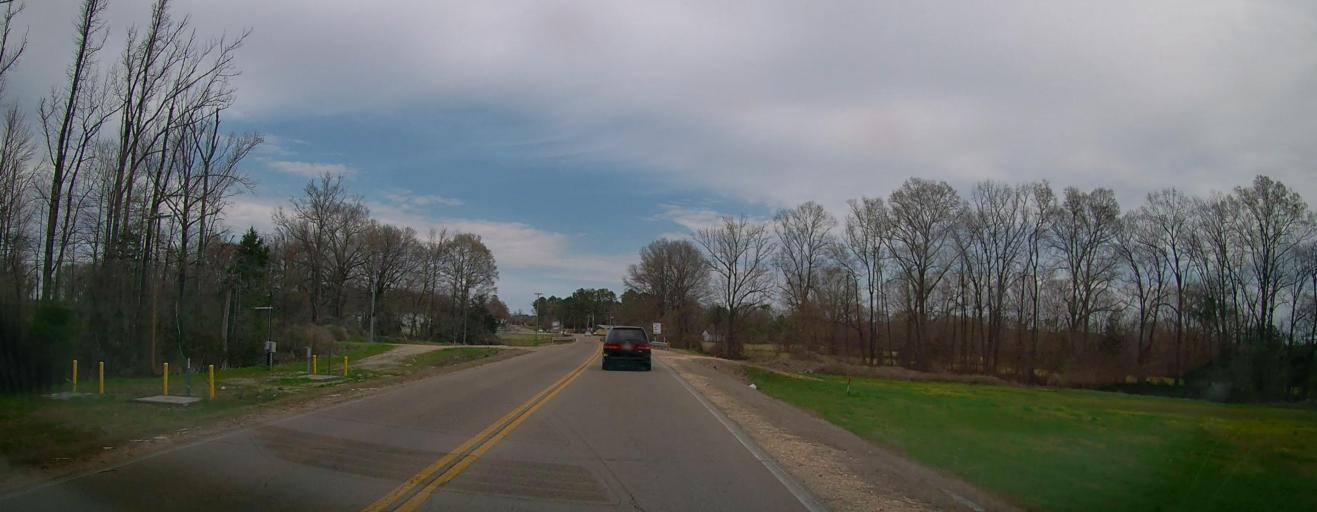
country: US
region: Mississippi
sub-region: Lee County
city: Plantersville
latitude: 34.2592
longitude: -88.6504
